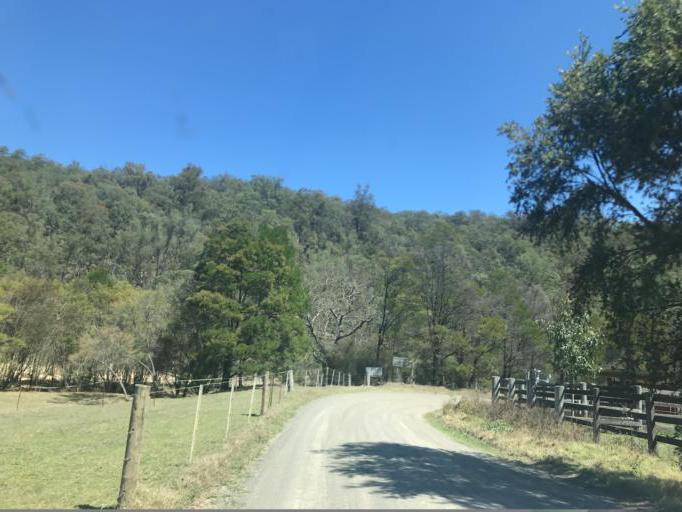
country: AU
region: New South Wales
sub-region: Wyong Shire
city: Little Jilliby
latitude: -33.2044
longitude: 150.9914
